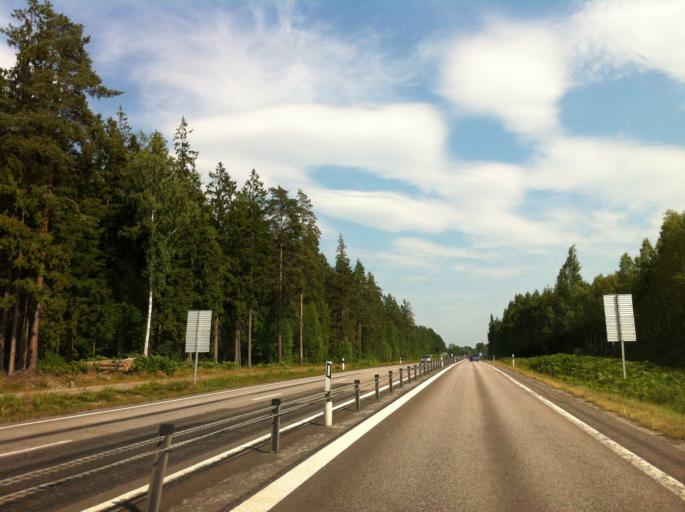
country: SE
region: Kalmar
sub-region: Kalmar Kommun
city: Trekanten
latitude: 56.7131
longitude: 16.0606
